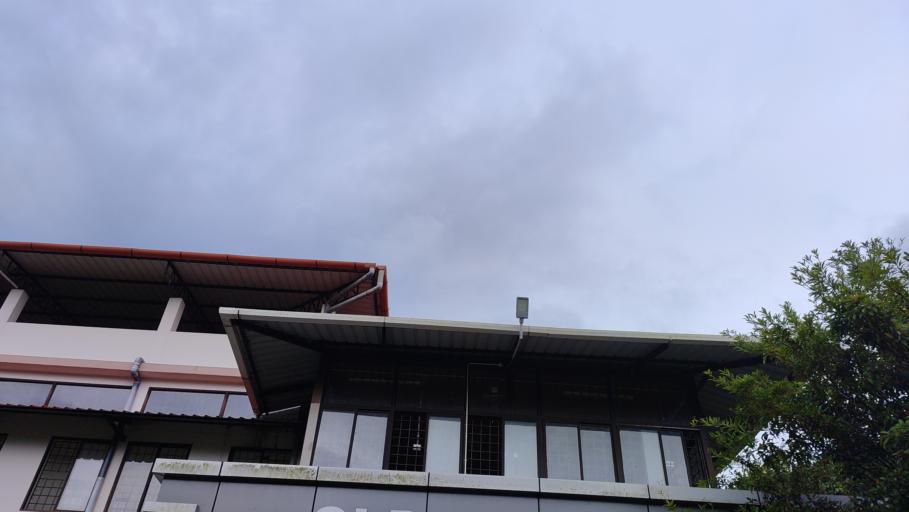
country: IN
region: Kerala
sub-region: Kasaragod District
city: Kasaragod
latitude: 12.4823
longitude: 75.0157
